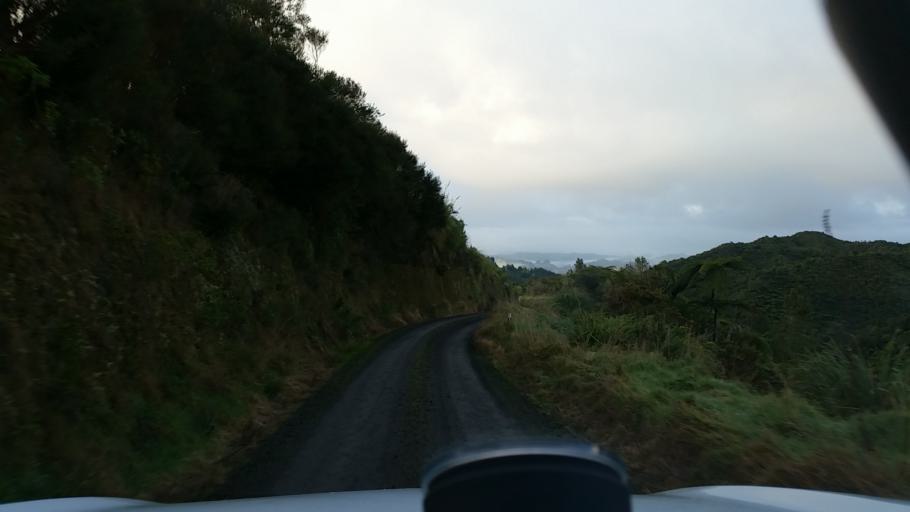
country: NZ
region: Taranaki
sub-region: South Taranaki District
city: Eltham
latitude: -39.4427
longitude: 174.4511
